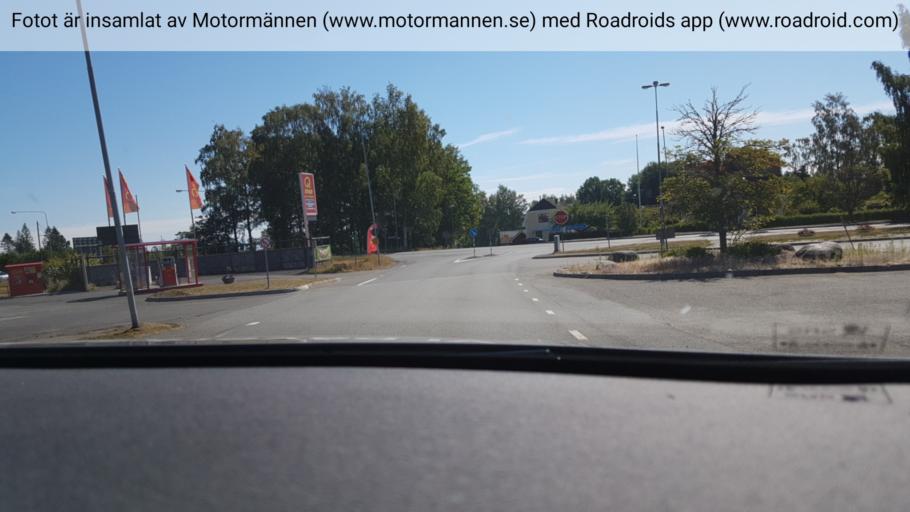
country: SE
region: Vaestra Goetaland
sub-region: Hjo Kommun
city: Hjo
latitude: 58.0968
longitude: 14.2044
